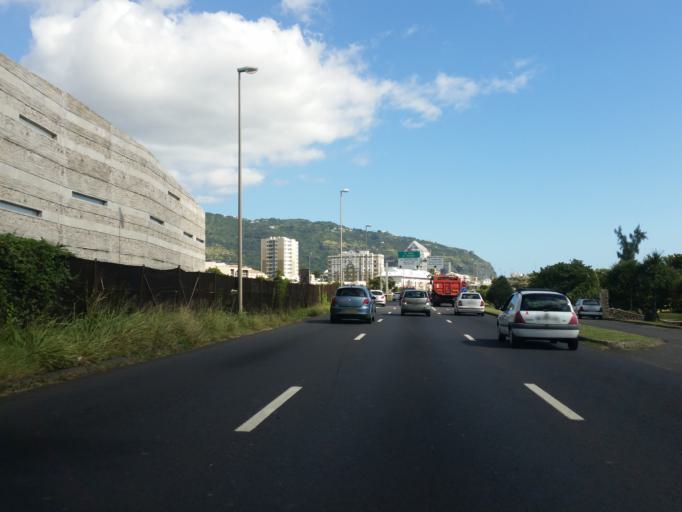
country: RE
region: Reunion
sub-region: Reunion
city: Saint-Denis
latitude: -20.8845
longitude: 55.4691
